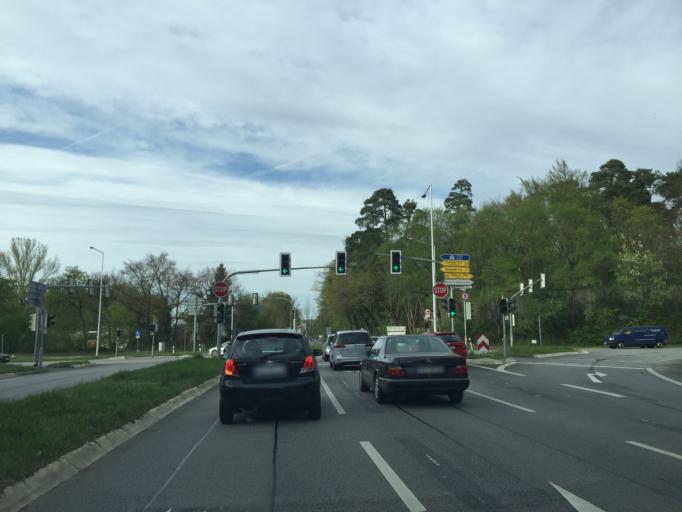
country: DE
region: Hesse
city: Pfungstadt
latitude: 49.8014
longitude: 8.6393
